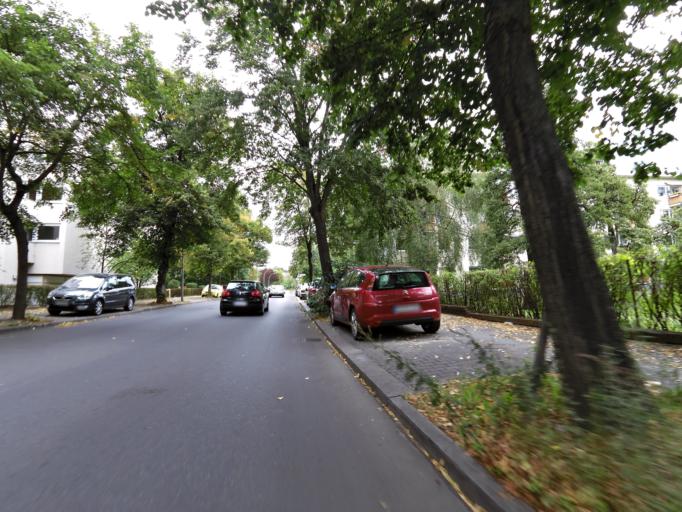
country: DE
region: Berlin
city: Mariendorf
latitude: 52.4476
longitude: 13.3707
